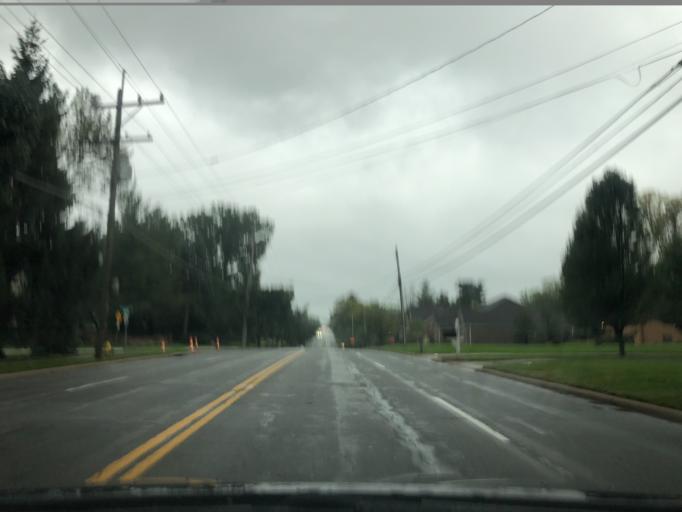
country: US
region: Ohio
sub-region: Hamilton County
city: Blue Ash
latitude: 39.2216
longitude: -84.3780
